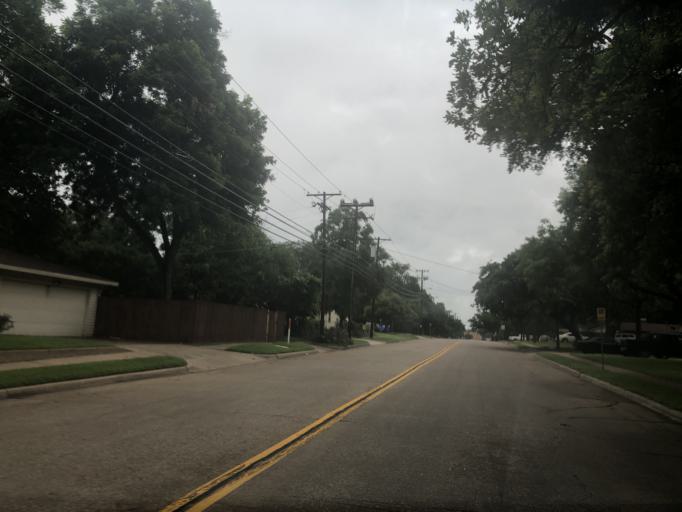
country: US
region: Texas
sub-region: Dallas County
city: Irving
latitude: 32.7976
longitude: -96.9469
